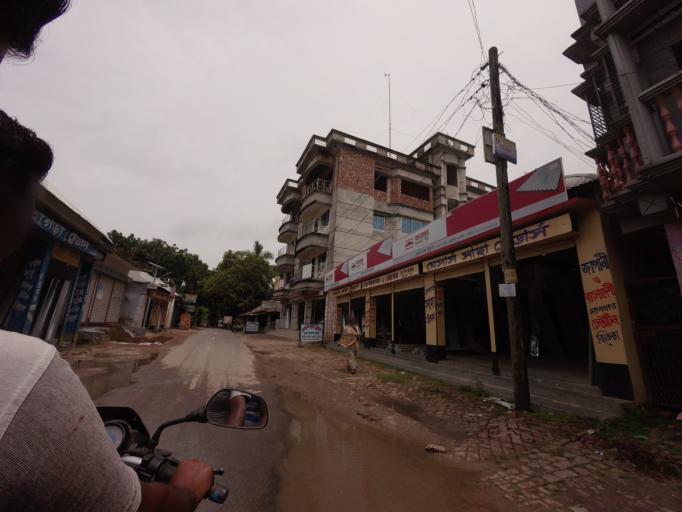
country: BD
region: Khulna
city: Kalia
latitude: 23.0859
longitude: 89.6691
